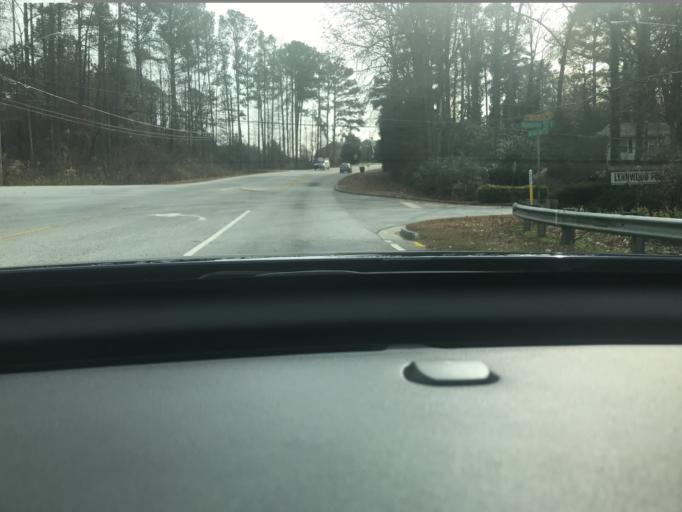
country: US
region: Georgia
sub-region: Gwinnett County
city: Mountain Park
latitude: 33.8617
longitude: -84.0971
